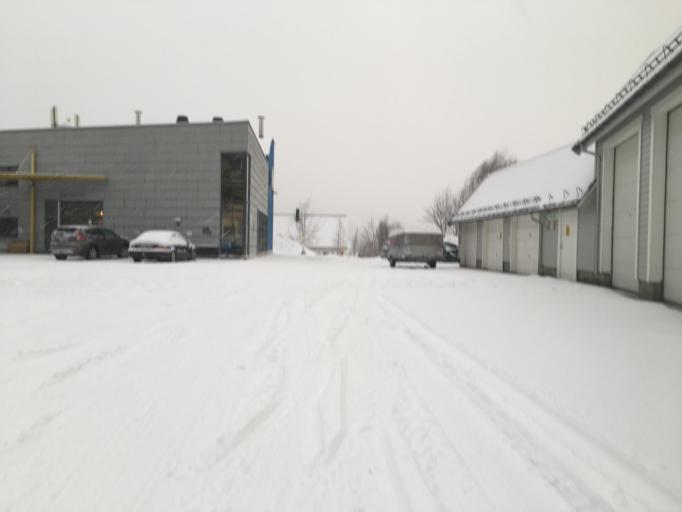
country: NO
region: Nordland
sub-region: Rana
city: Mo i Rana
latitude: 66.3321
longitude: 14.1571
